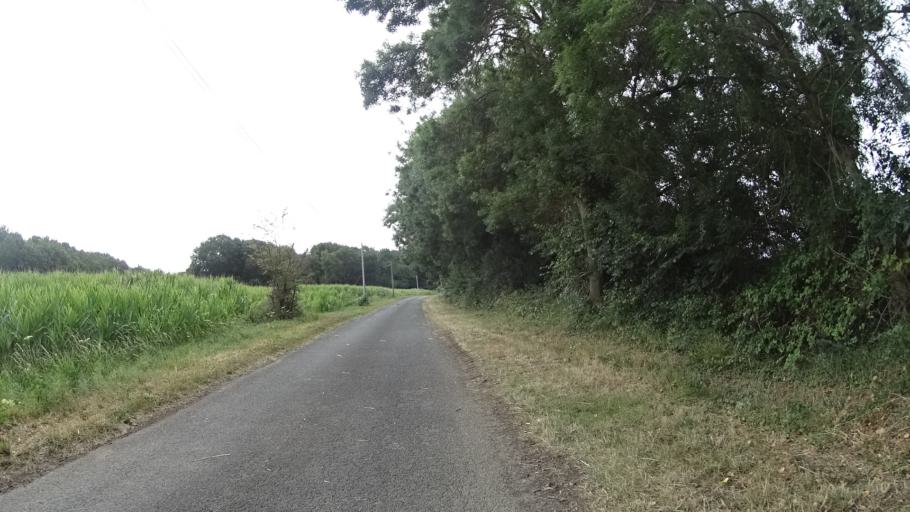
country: FR
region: Pays de la Loire
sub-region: Departement de Maine-et-Loire
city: Montjean-sur-Loire
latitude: 47.3821
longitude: -0.8320
